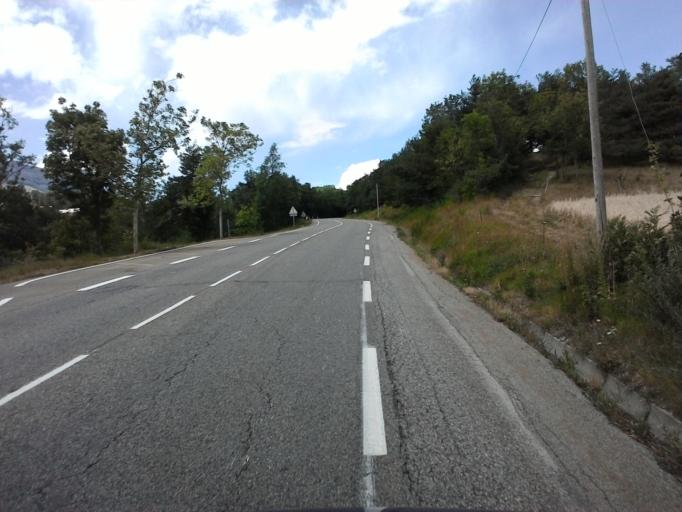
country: FR
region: Provence-Alpes-Cote d'Azur
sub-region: Departement des Hautes-Alpes
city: Gap
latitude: 44.5931
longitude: 6.0808
